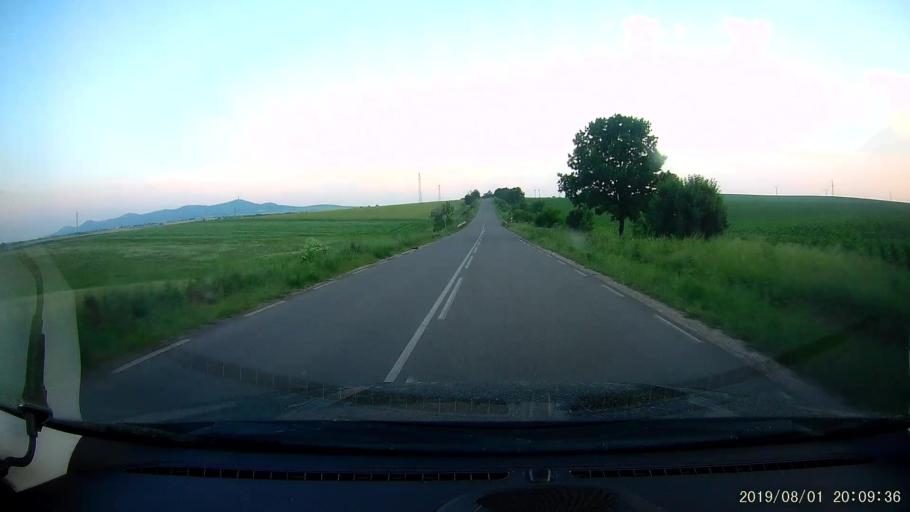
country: BG
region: Yambol
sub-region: Obshtina Yambol
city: Yambol
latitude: 42.4961
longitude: 26.5931
